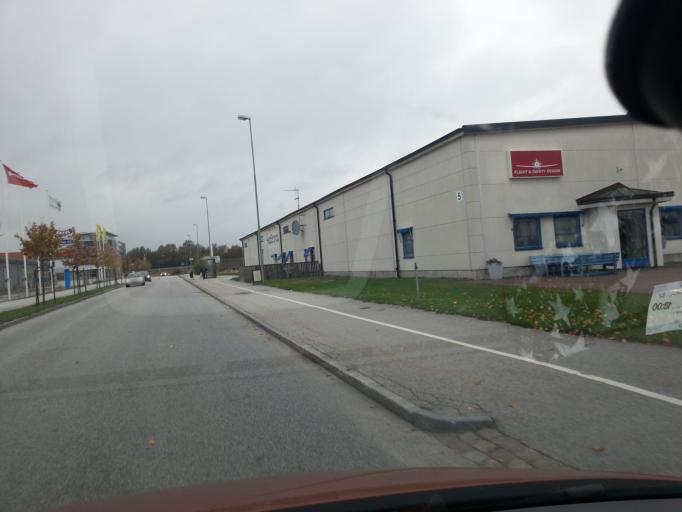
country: SE
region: Skane
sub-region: Lunds Kommun
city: Lund
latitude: 55.6906
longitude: 13.2128
